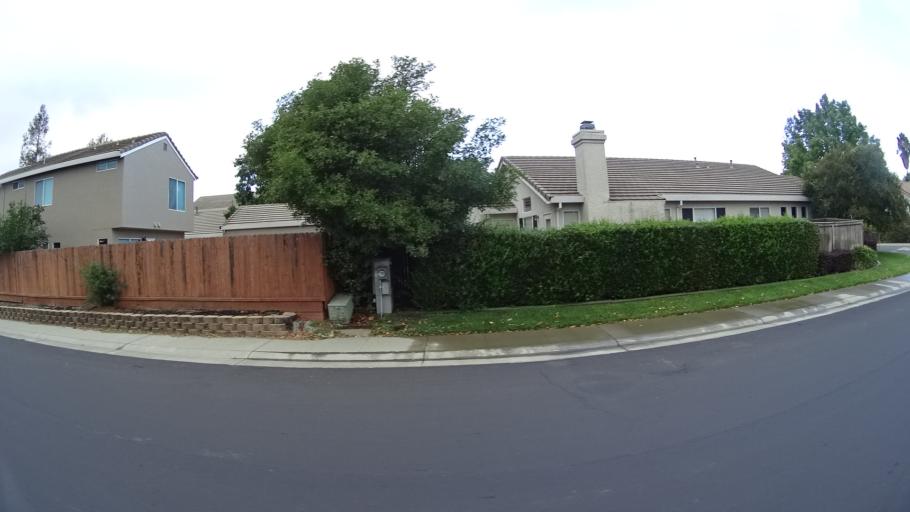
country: US
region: California
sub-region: Sacramento County
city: Laguna
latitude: 38.4328
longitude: -121.4216
